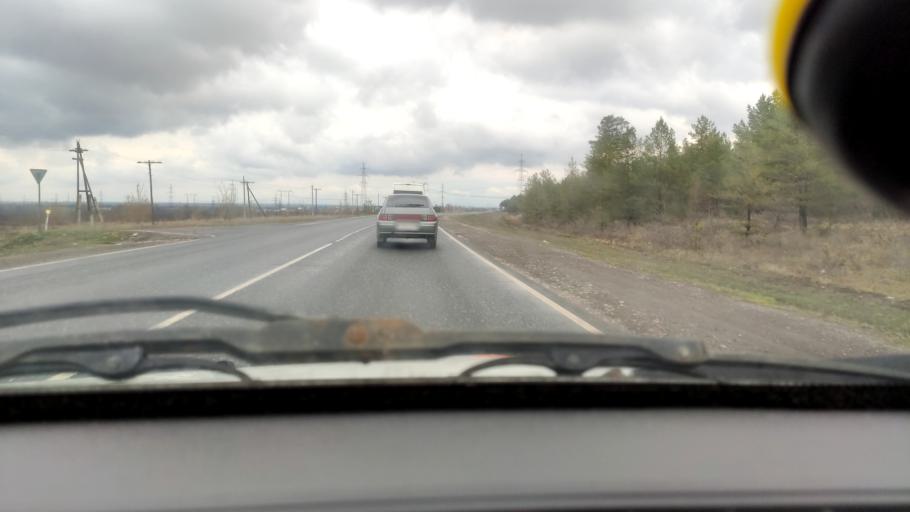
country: RU
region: Samara
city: Zhigulevsk
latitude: 53.5717
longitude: 49.5525
